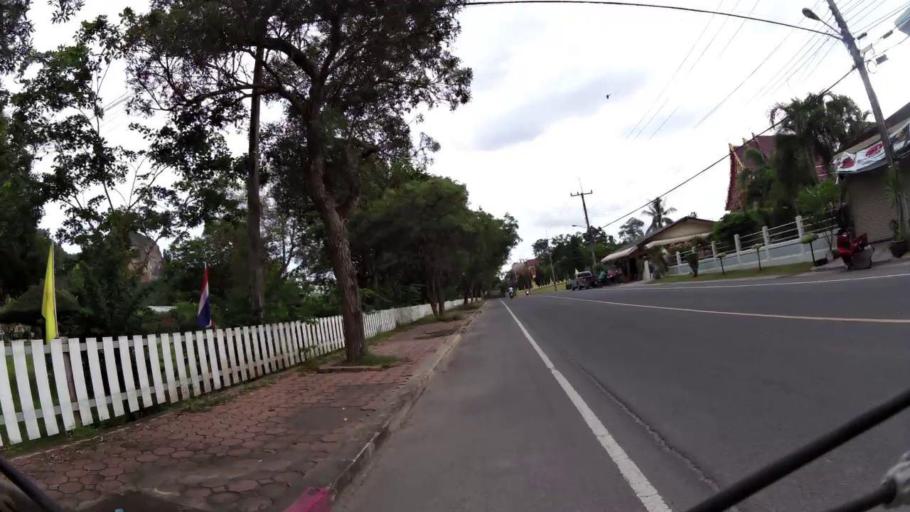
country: TH
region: Prachuap Khiri Khan
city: Prachuap Khiri Khan
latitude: 11.7516
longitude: 99.7901
